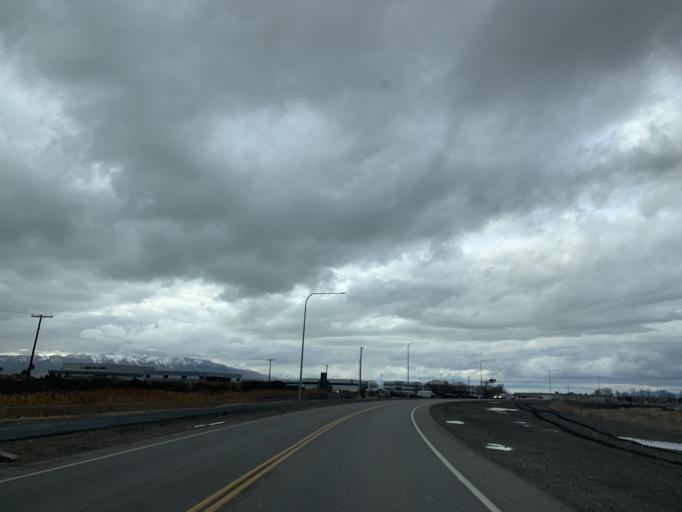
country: US
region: Utah
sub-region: Utah County
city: Provo
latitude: 40.2155
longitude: -111.7109
